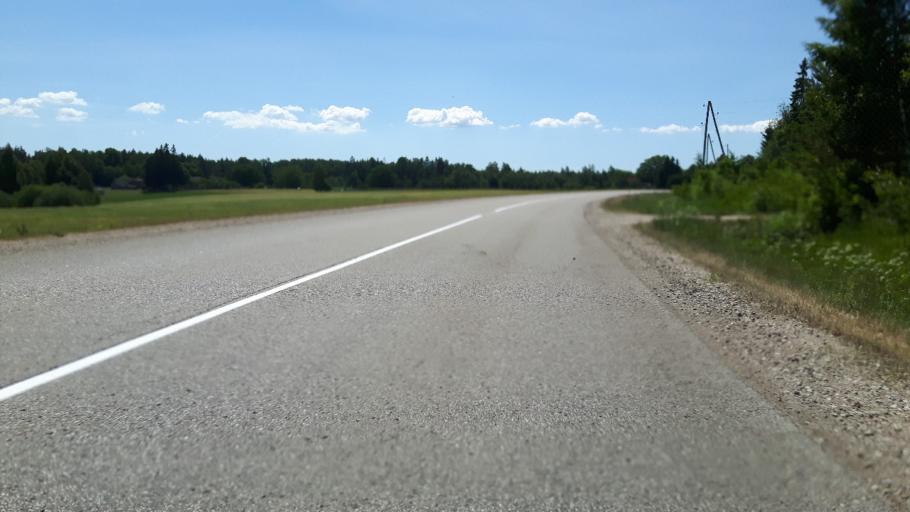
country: LV
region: Kuldigas Rajons
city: Kuldiga
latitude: 56.9088
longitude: 21.9044
